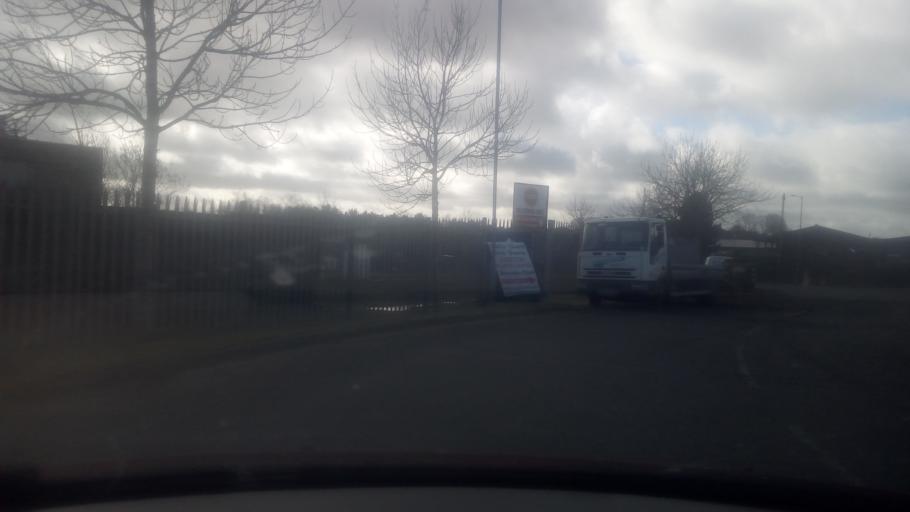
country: GB
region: Scotland
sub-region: The Scottish Borders
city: Saint Boswells
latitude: 55.5599
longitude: -2.6550
